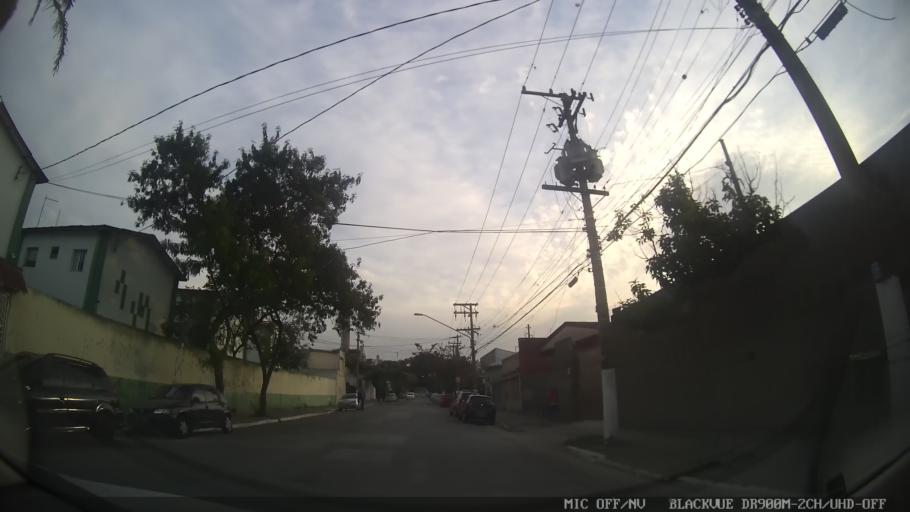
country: BR
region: Sao Paulo
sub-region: Sao Caetano Do Sul
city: Sao Caetano do Sul
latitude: -23.6017
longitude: -46.5871
